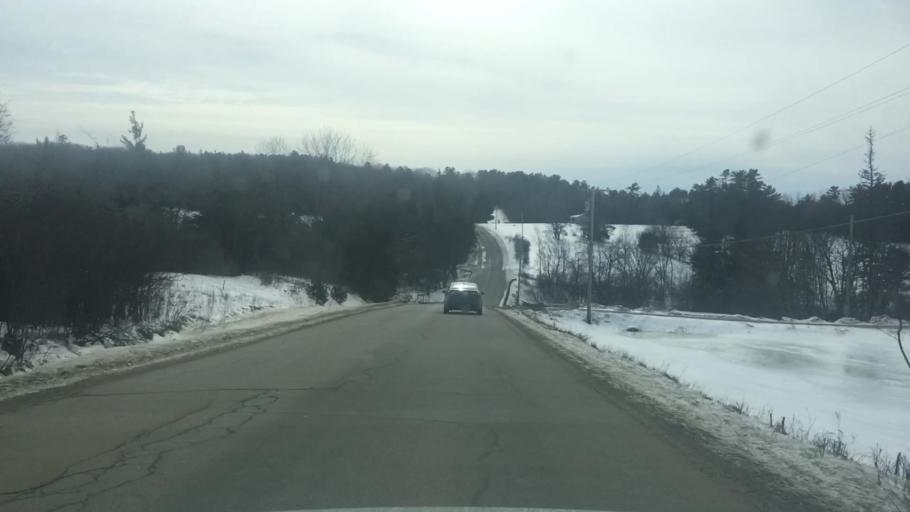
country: US
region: Maine
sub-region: Hancock County
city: Orland
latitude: 44.5950
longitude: -68.7243
